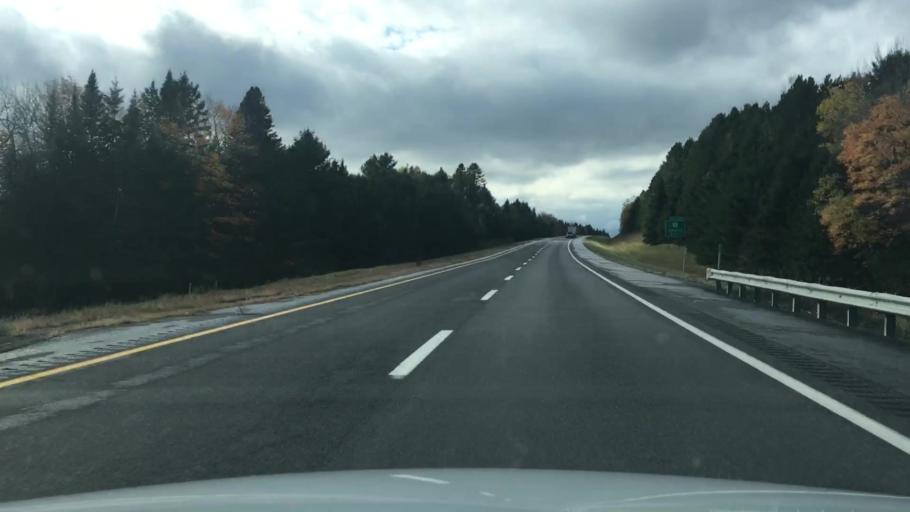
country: US
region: Maine
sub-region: Aroostook County
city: Hodgdon
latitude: 46.1406
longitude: -68.0122
